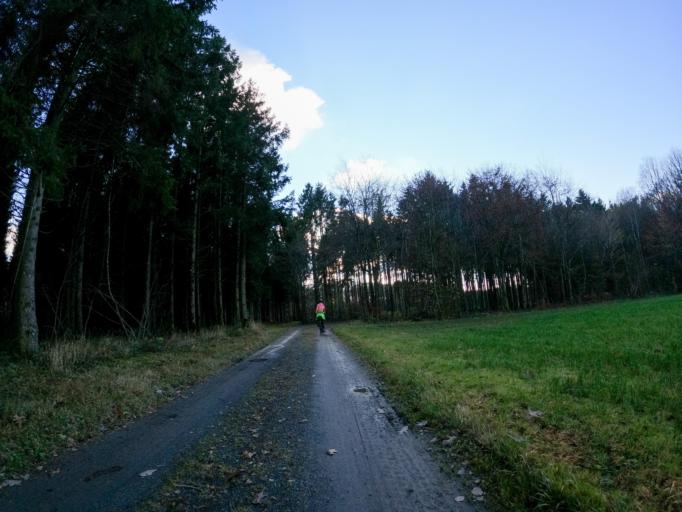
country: LU
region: Diekirch
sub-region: Canton de Wiltz
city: Bavigne
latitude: 49.9752
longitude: 5.8295
